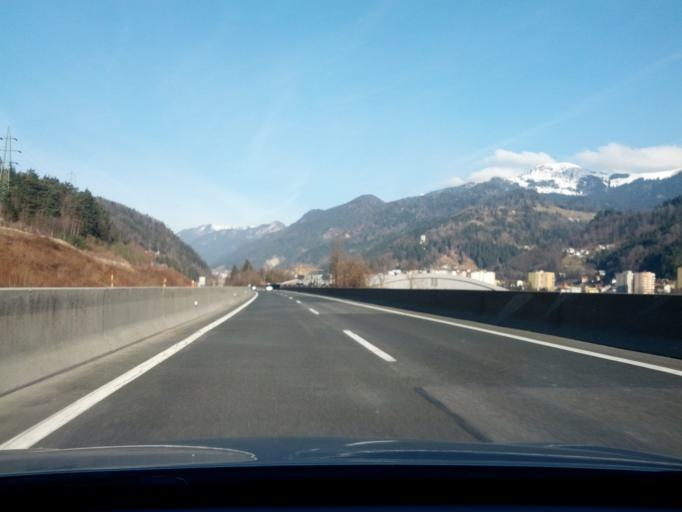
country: SI
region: Jesenice
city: Jesenice
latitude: 46.4310
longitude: 14.0535
